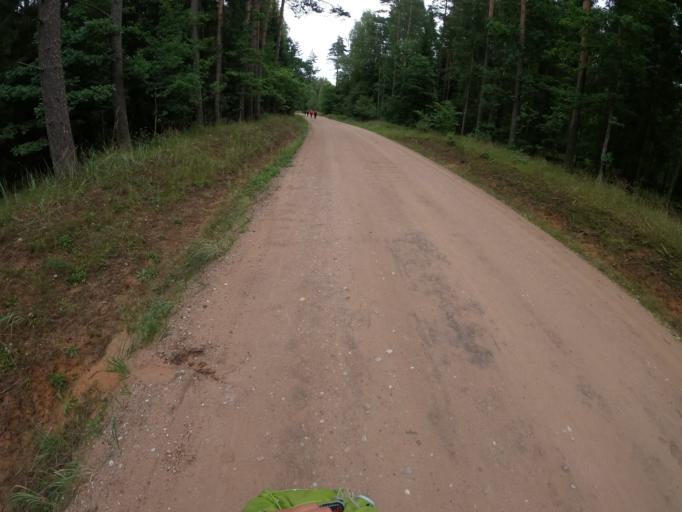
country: LV
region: Kuldigas Rajons
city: Kuldiga
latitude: 57.0120
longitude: 21.9838
